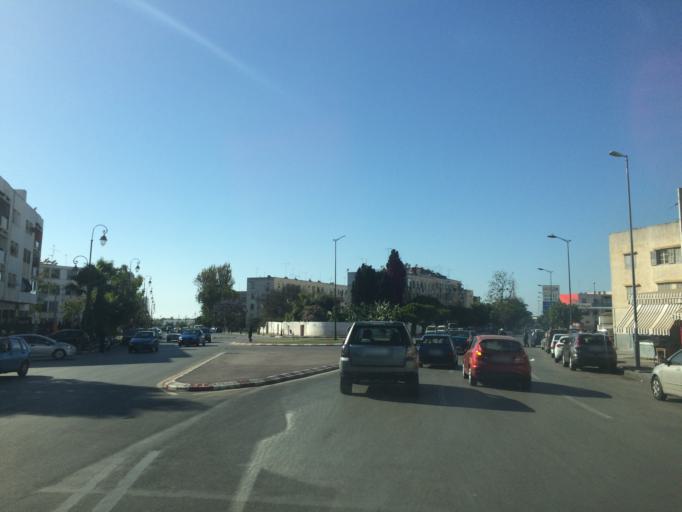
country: MA
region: Rabat-Sale-Zemmour-Zaer
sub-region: Rabat
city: Rabat
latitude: 33.9938
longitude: -6.8184
